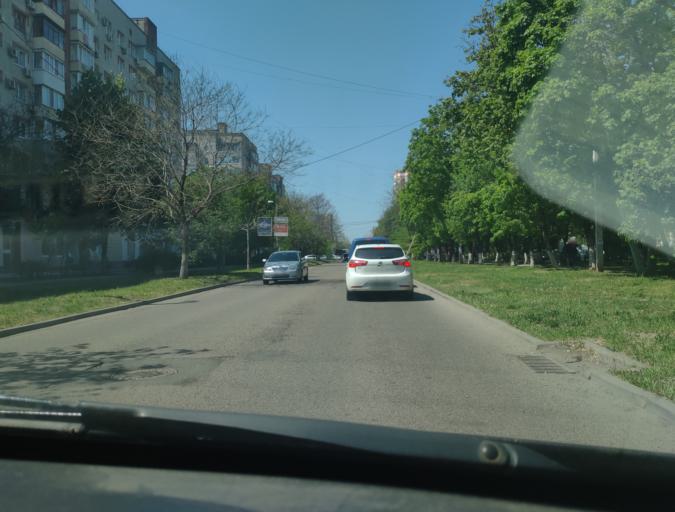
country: RU
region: Krasnodarskiy
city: Krasnodar
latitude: 45.0625
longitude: 39.0056
